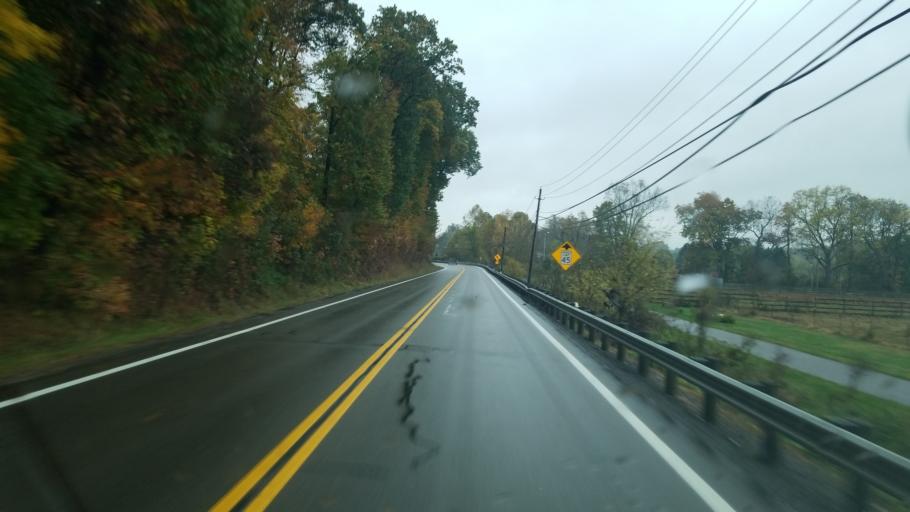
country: US
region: Ohio
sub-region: Coshocton County
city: Coshocton
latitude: 40.2932
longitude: -81.8726
